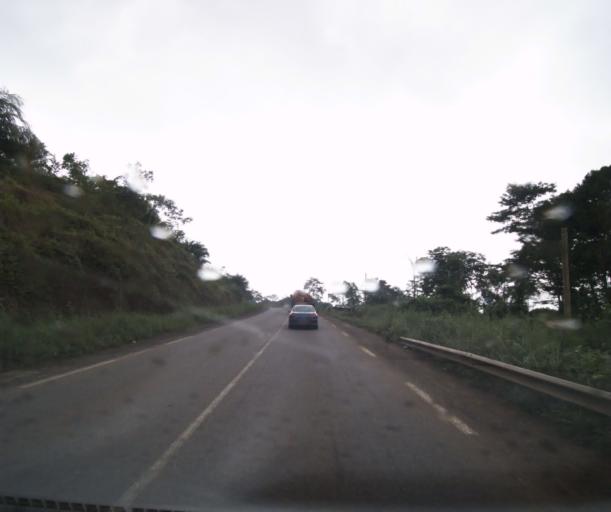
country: CM
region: Littoral
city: Edea
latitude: 3.7922
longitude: 10.2096
